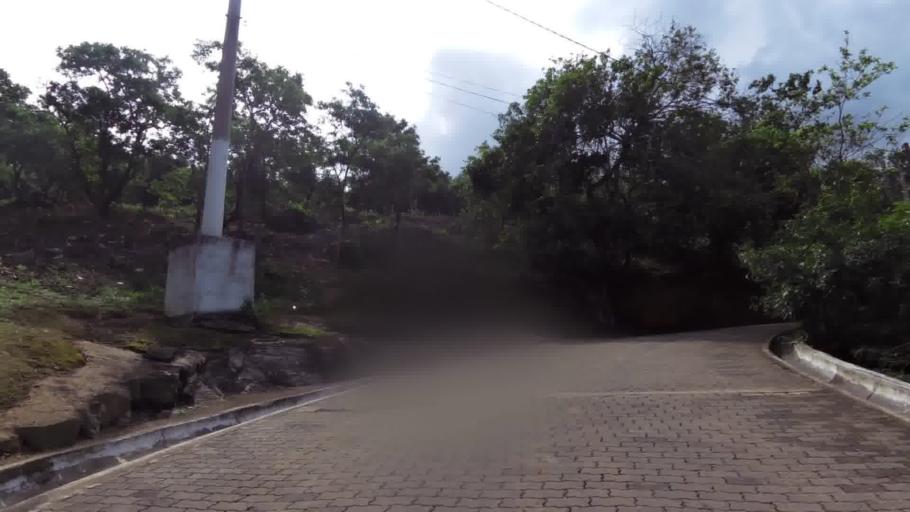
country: BR
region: Espirito Santo
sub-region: Piuma
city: Piuma
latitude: -20.8098
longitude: -40.6616
